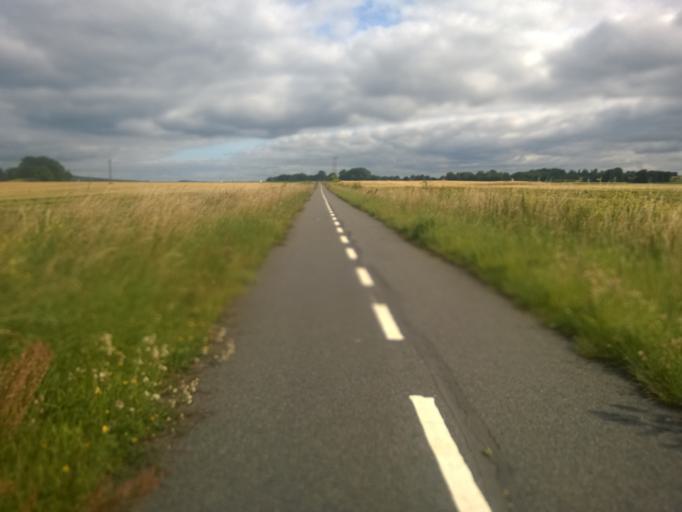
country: SE
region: Skane
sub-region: Kristianstads Kommun
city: Kristianstad
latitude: 56.0665
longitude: 14.1917
